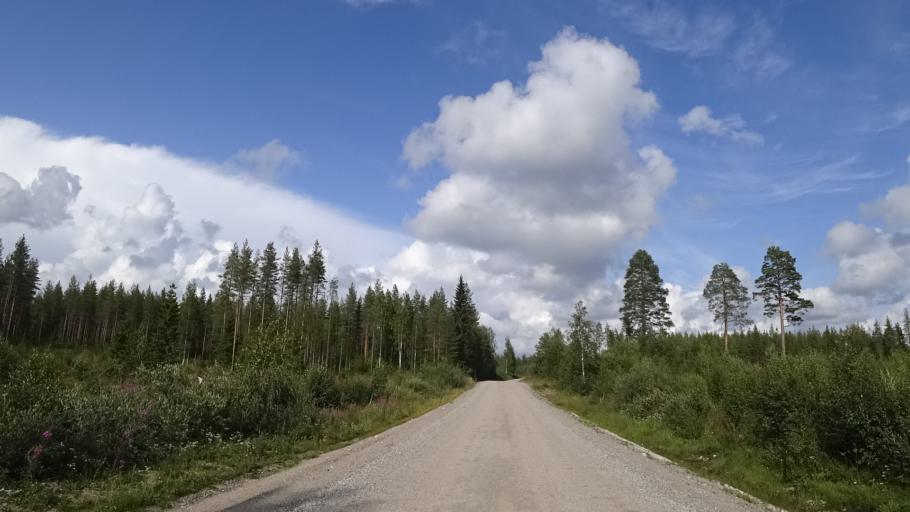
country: FI
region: North Karelia
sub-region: Pielisen Karjala
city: Lieksa
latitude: 63.5774
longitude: 30.1250
